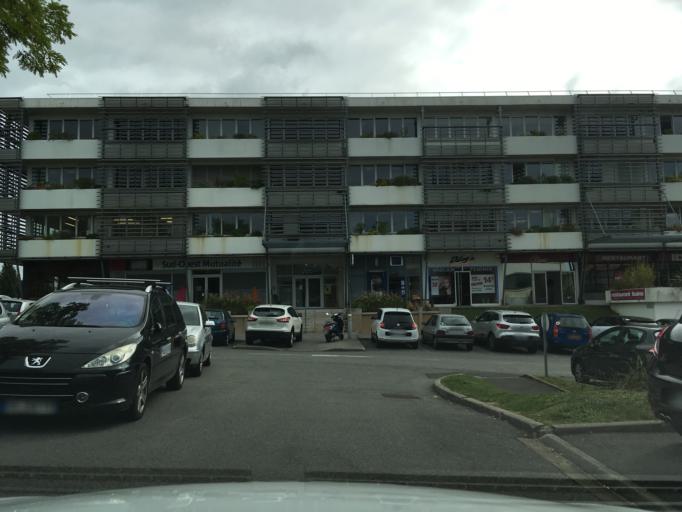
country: FR
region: Aquitaine
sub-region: Departement des Pyrenees-Atlantiques
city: Anglet
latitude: 43.4952
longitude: -1.5141
